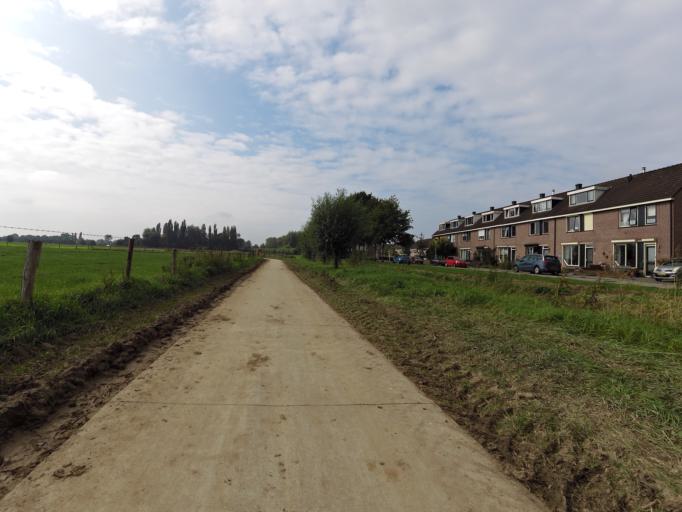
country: NL
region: Gelderland
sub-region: Gemeente Westervoort
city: Westervoort
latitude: 51.9424
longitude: 5.9786
